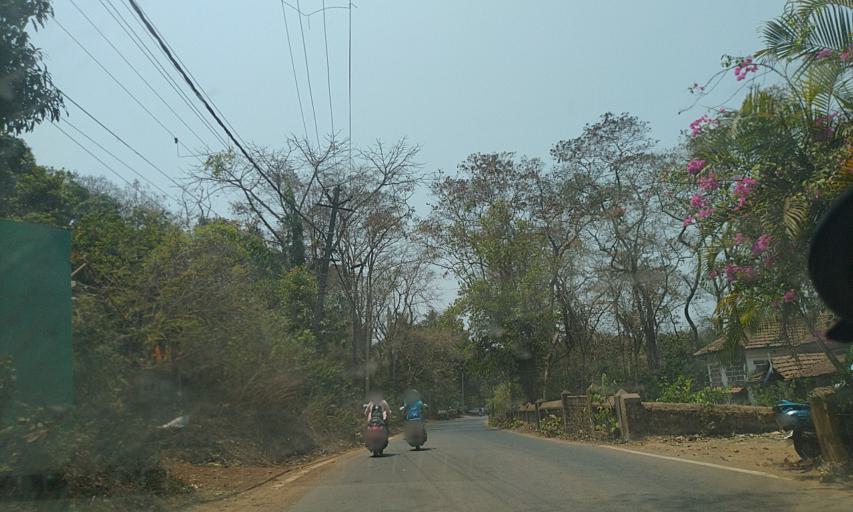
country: IN
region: Goa
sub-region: North Goa
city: Mapuca
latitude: 15.5972
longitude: 73.7870
